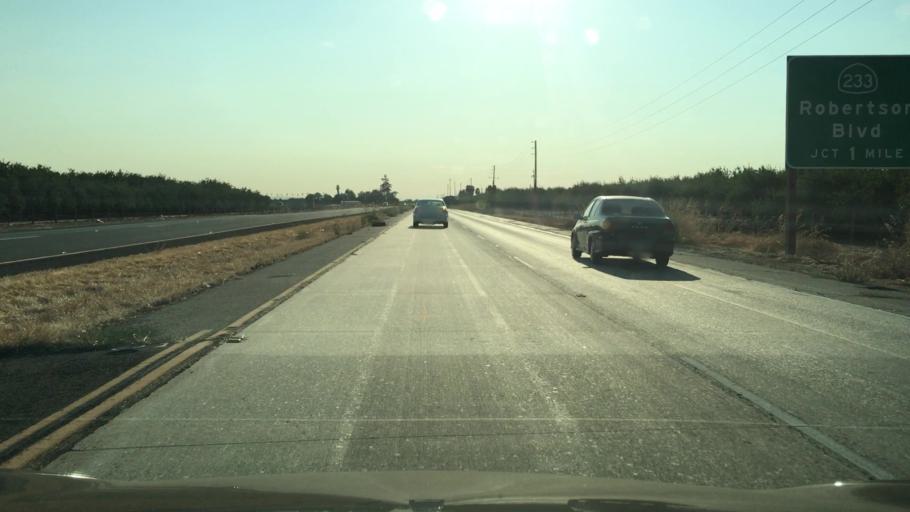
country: US
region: California
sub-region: Madera County
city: Chowchilla
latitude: 37.0836
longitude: -120.2766
